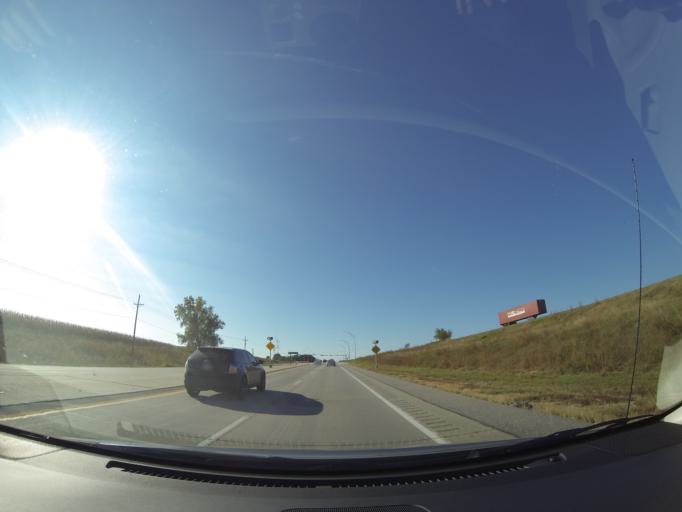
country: US
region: Nebraska
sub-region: Sarpy County
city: Gretna
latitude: 41.1926
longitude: -96.2344
